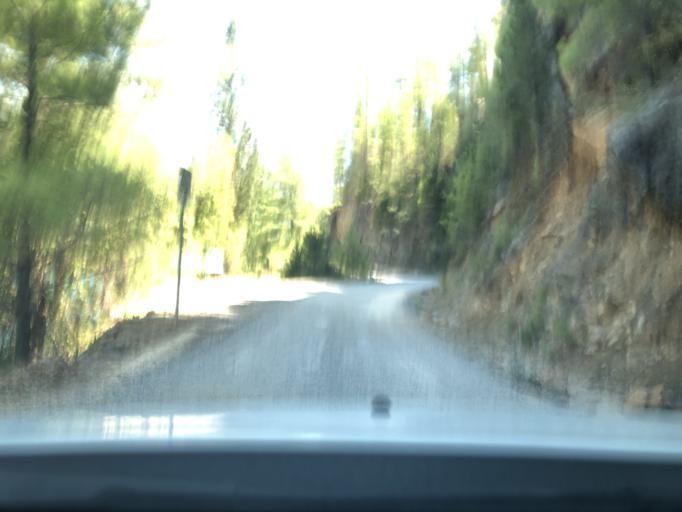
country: TR
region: Antalya
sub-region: Manavgat
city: Manavgat
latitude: 36.9063
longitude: 31.5573
